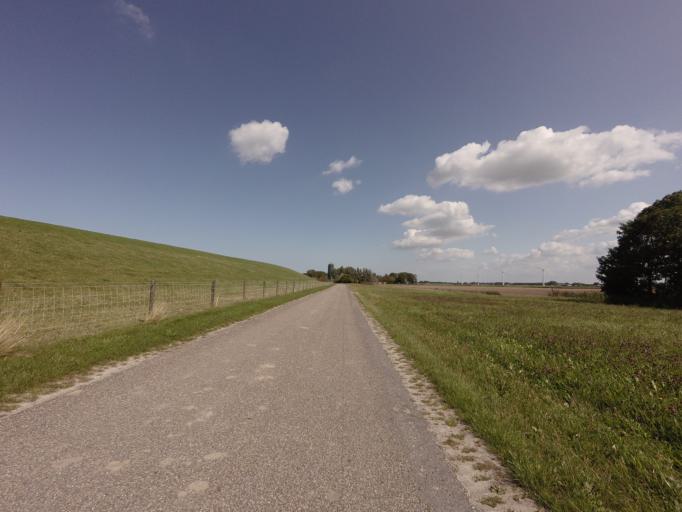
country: NL
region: Friesland
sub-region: Gemeente Ferwerderadiel
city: Hallum
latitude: 53.3261
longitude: 5.7688
